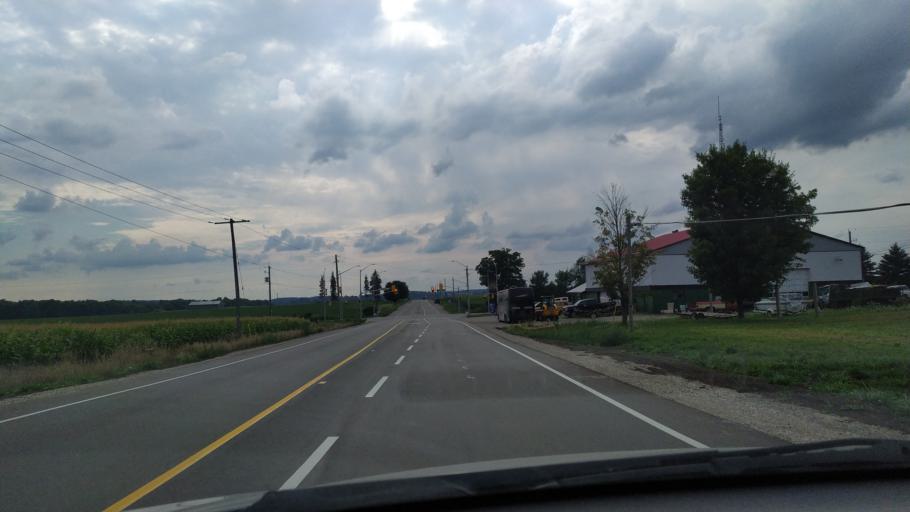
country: CA
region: Ontario
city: Kitchener
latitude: 43.3541
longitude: -80.5043
